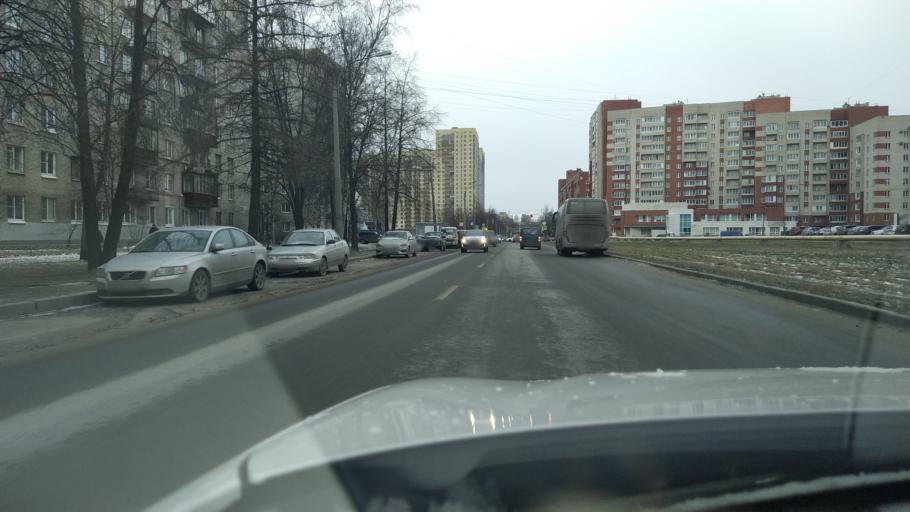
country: RU
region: Leningrad
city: Akademicheskoe
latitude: 60.0061
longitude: 30.4010
